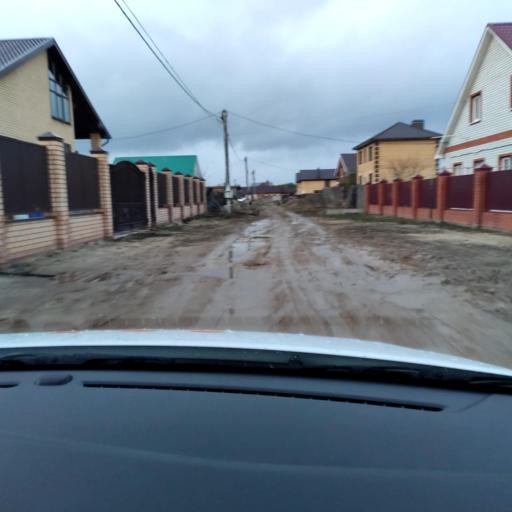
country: RU
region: Tatarstan
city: Stolbishchi
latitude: 55.6928
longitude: 49.1543
